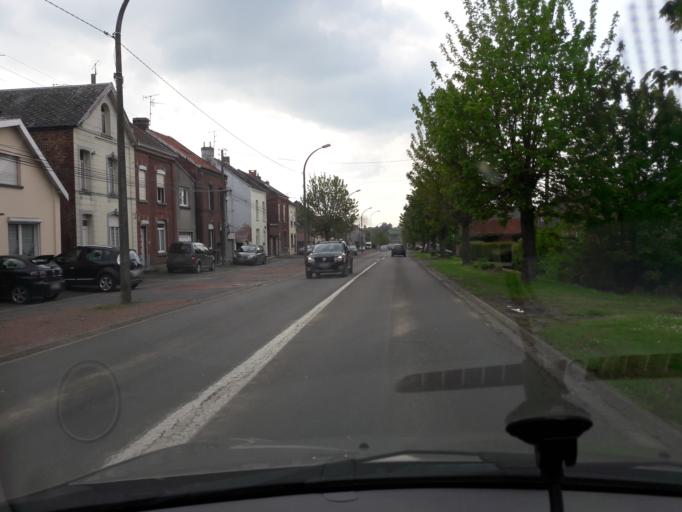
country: FR
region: Nord-Pas-de-Calais
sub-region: Departement du Nord
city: Ferriere-la-Grande
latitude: 50.2601
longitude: 4.0043
